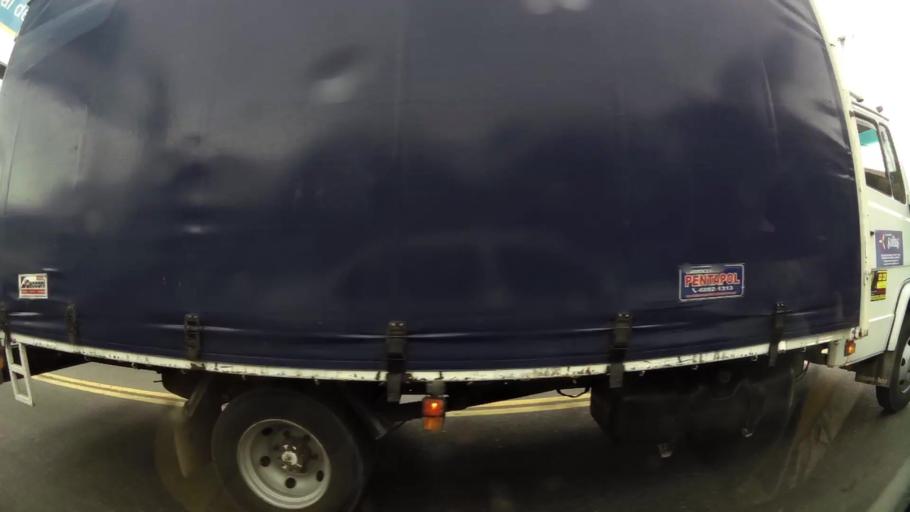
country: AR
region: Buenos Aires
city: San Justo
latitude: -34.6635
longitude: -58.5207
